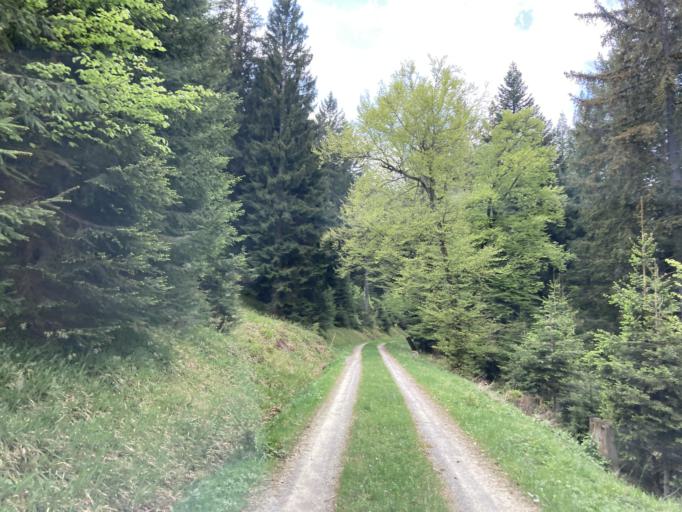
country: DE
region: Baden-Wuerttemberg
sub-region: Karlsruhe Region
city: Biberach
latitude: 48.5171
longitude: 8.2767
